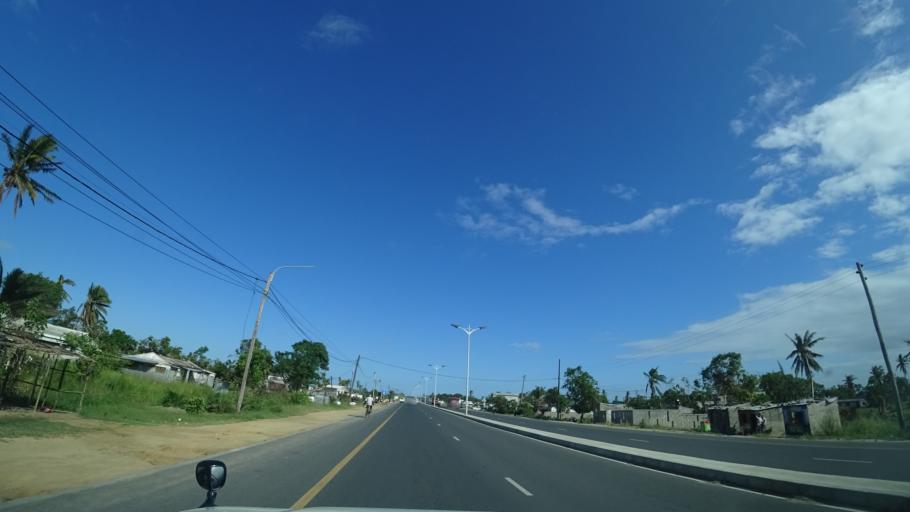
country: MZ
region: Sofala
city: Beira
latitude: -19.7402
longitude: 34.8588
